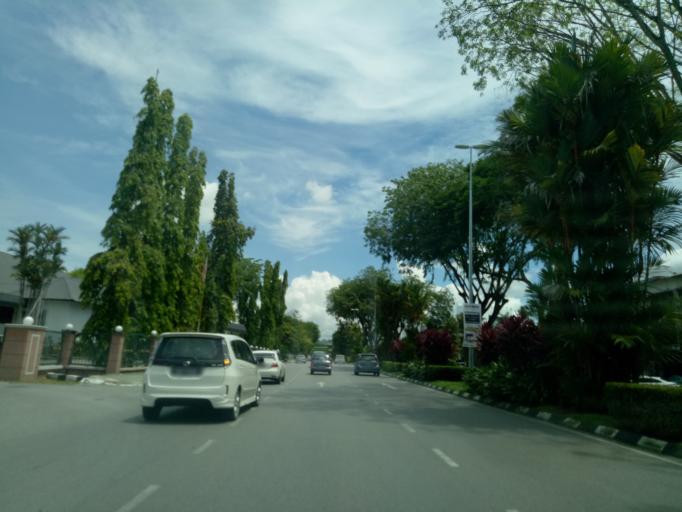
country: MY
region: Sarawak
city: Kuching
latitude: 1.5522
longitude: 110.3638
